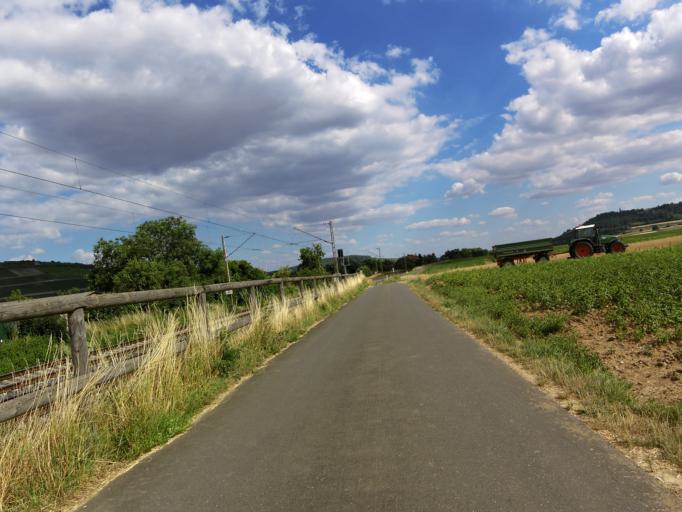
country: DE
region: Bavaria
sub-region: Regierungsbezirk Unterfranken
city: Randersacker
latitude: 49.7534
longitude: 9.9752
